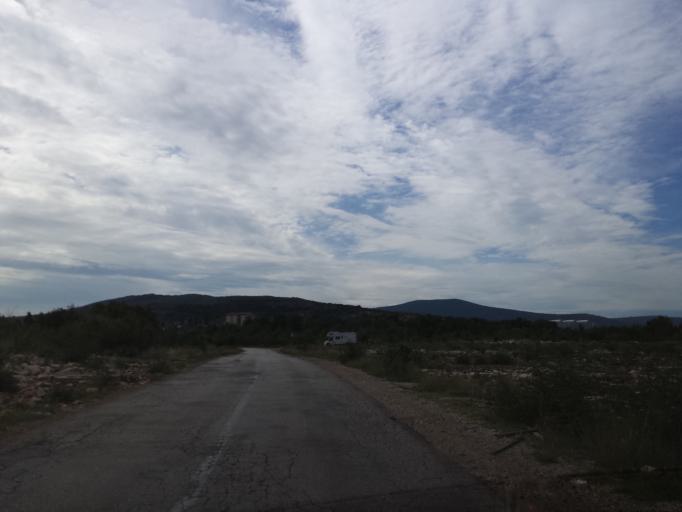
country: BA
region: Federation of Bosnia and Herzegovina
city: Capljina
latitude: 43.1736
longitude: 17.6494
